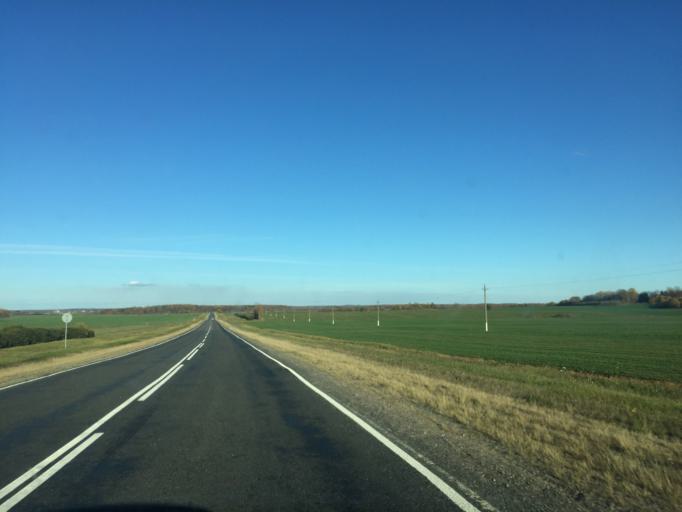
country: BY
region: Vitebsk
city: Dzisna
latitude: 55.3062
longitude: 28.2561
